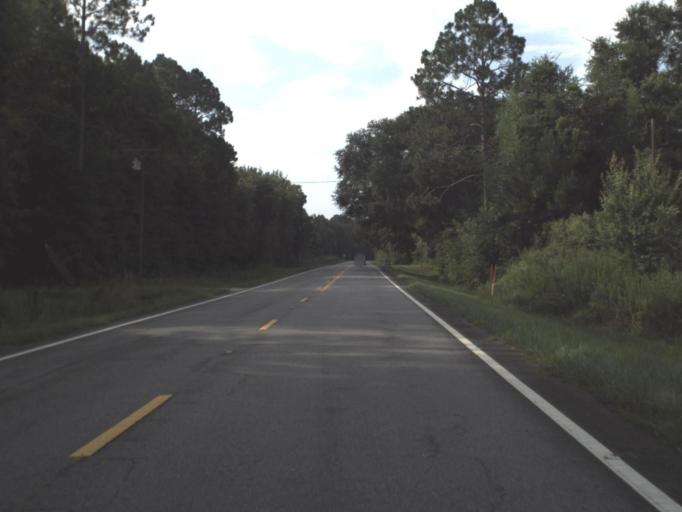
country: US
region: Florida
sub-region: Taylor County
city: Perry
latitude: 30.3464
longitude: -83.6489
